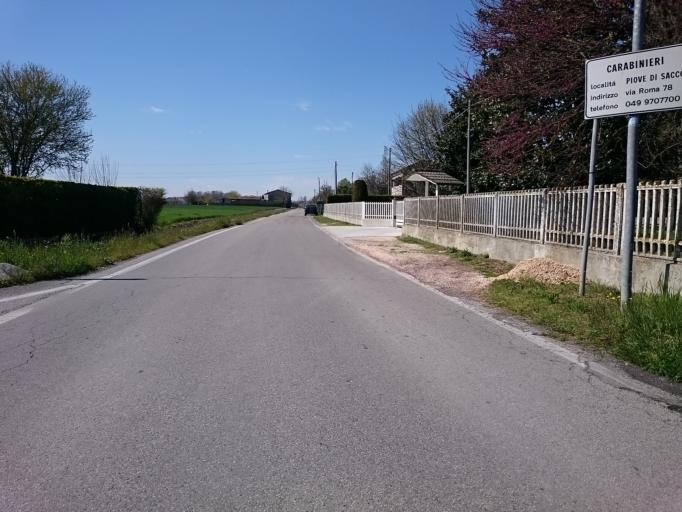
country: IT
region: Veneto
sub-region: Provincia di Padova
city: Campagnola
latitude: 45.2895
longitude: 12.0128
